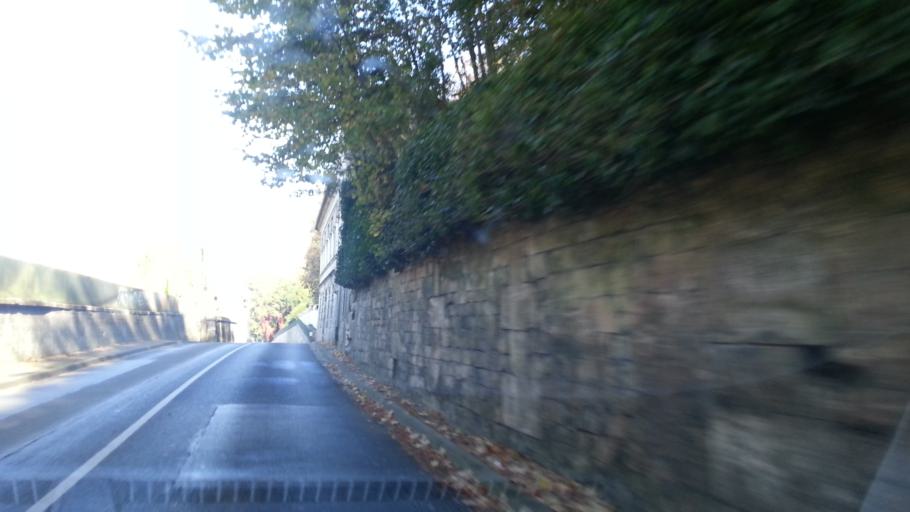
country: FR
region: Picardie
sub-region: Departement de l'Oise
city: Cires-les-Mello
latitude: 49.2703
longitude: 2.3658
